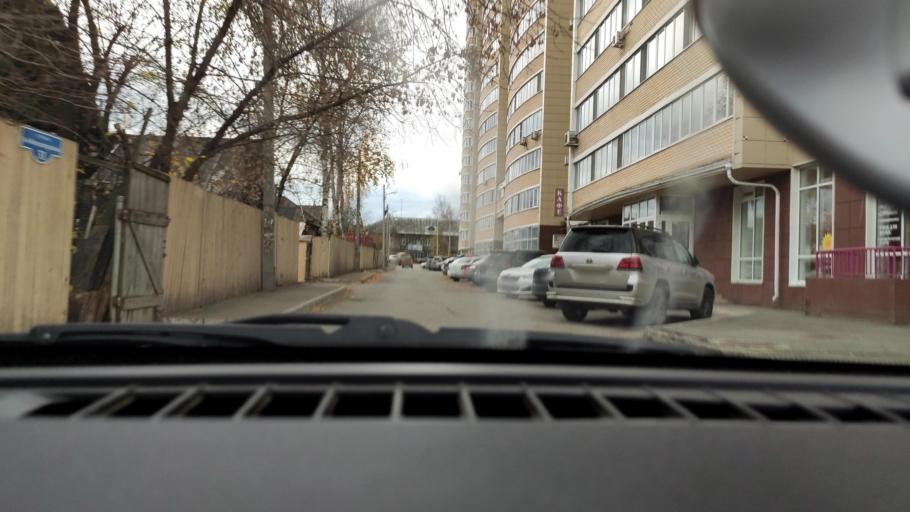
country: RU
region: Perm
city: Perm
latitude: 57.9747
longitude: 56.2050
